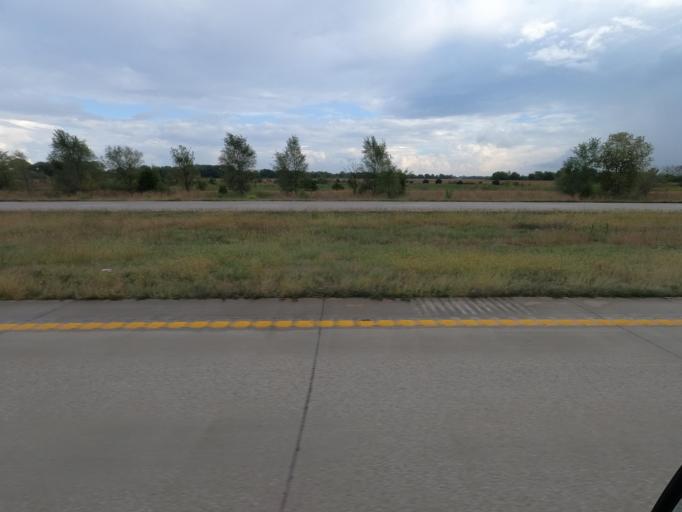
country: US
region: Missouri
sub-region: Clark County
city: Kahoka
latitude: 40.3828
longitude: -91.5813
